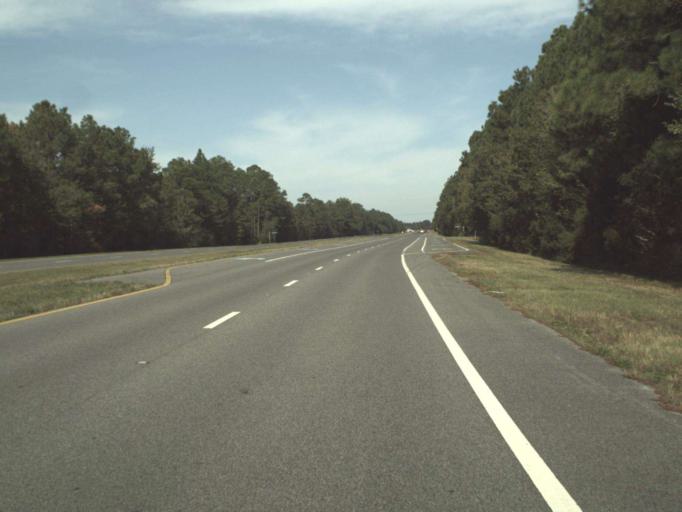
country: US
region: Florida
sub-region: Escambia County
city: Warrington
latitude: 30.3471
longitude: -87.3518
